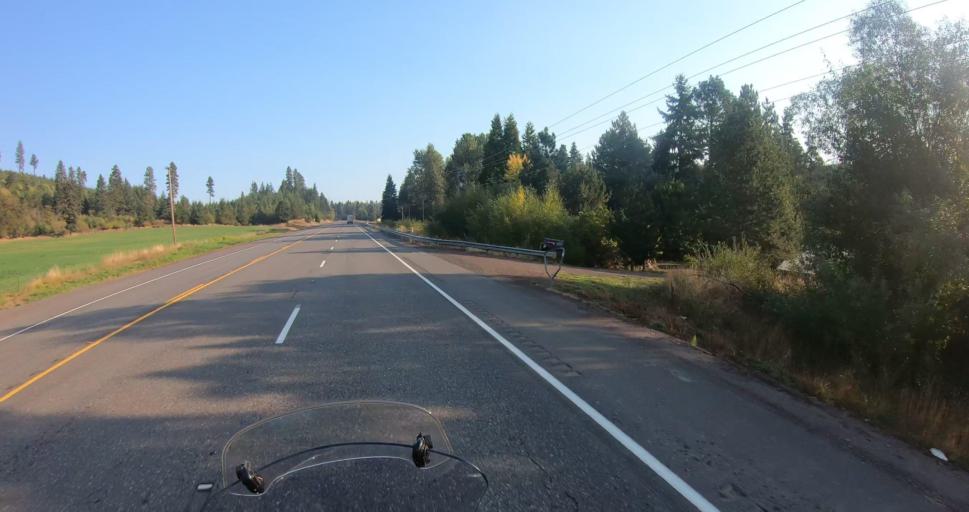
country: US
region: Oregon
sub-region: Hood River County
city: Odell
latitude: 45.5655
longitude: -121.5598
